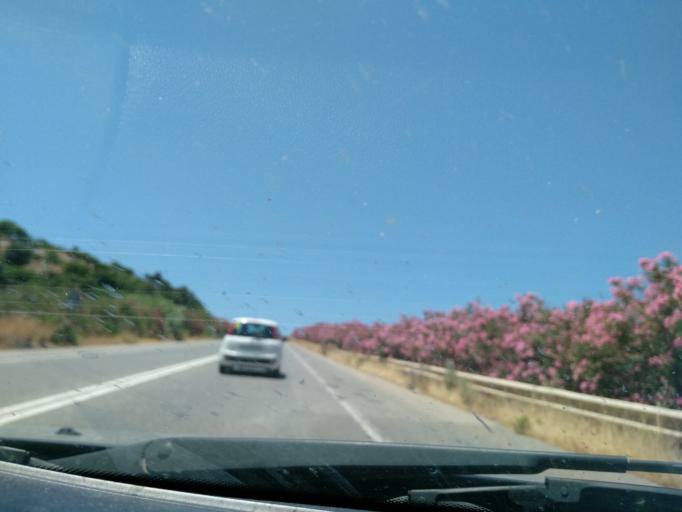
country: GR
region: Crete
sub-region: Nomos Rethymnis
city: Perama
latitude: 35.4086
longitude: 24.8112
